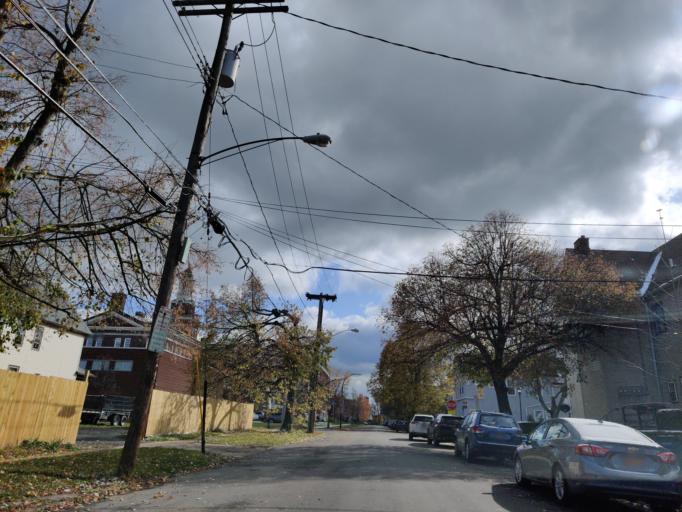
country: US
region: New York
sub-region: Erie County
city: Buffalo
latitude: 42.9047
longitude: -78.8868
